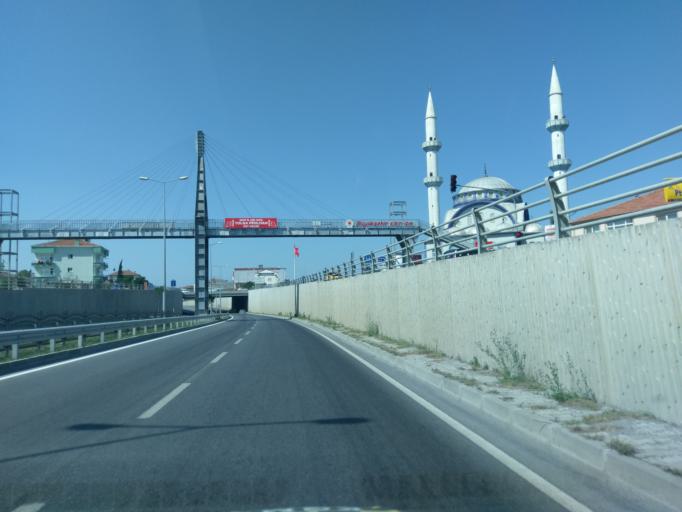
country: TR
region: Samsun
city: Bafra
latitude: 41.5506
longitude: 35.9260
